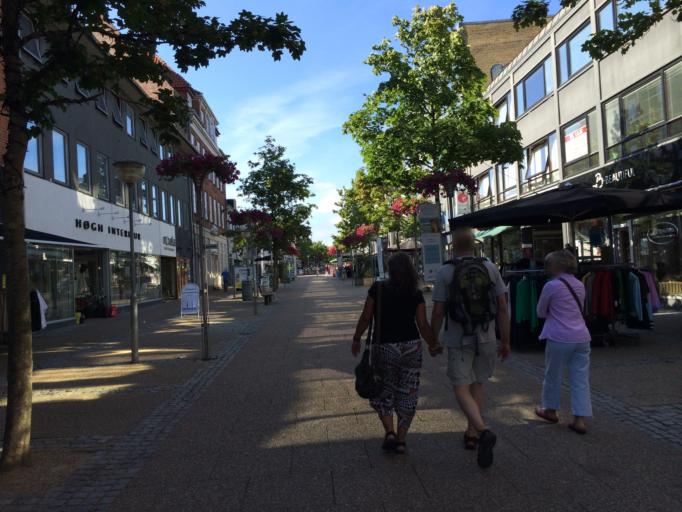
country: DK
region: North Denmark
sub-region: Hjorring Kommune
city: Hjorring
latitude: 57.4603
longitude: 9.9865
